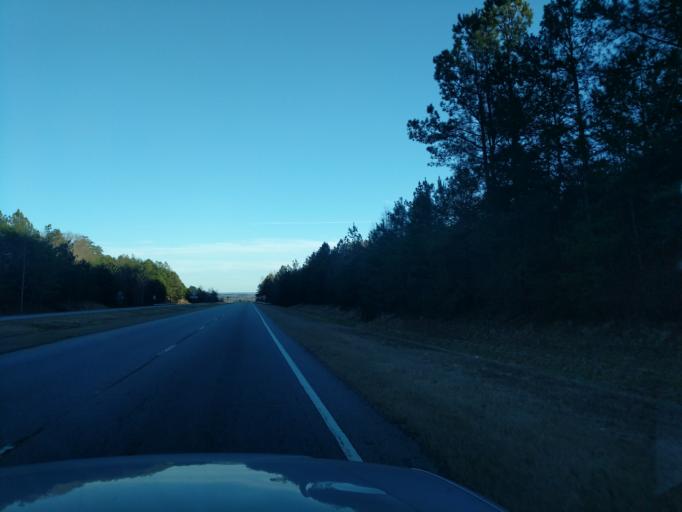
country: US
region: Georgia
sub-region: Stephens County
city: Toccoa
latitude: 34.5596
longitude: -83.3895
